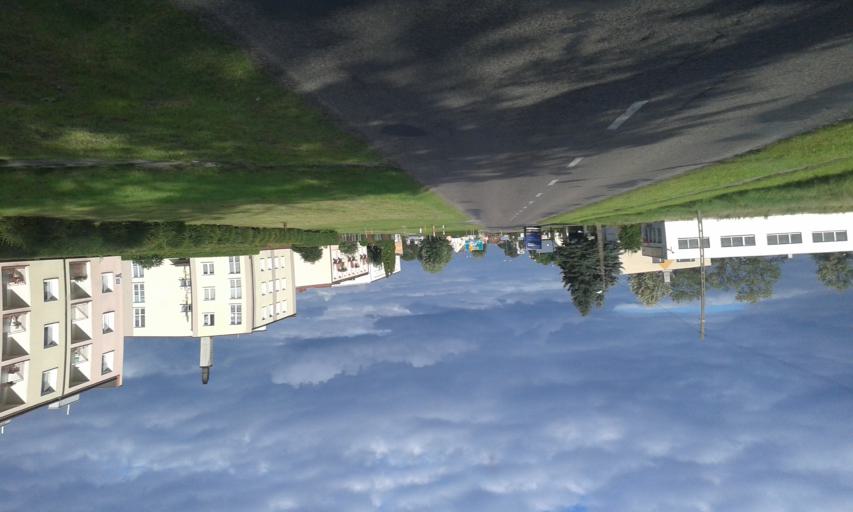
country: PL
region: West Pomeranian Voivodeship
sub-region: Powiat bialogardzki
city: Tychowo
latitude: 53.9243
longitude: 16.2487
